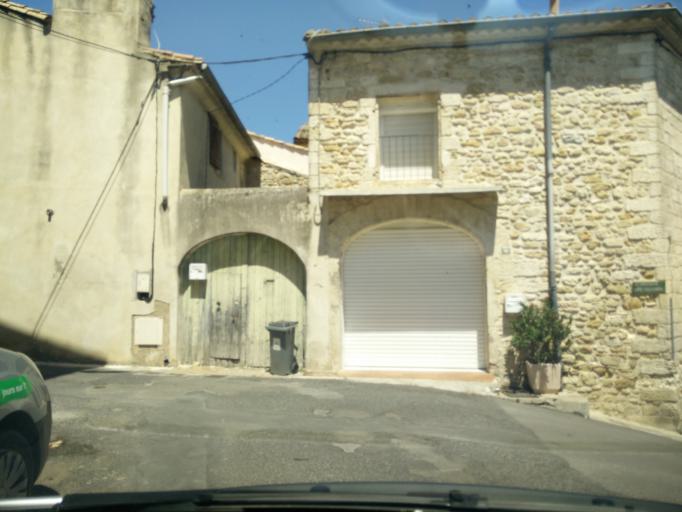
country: FR
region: Languedoc-Roussillon
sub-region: Departement de l'Herault
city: Saint-Christol
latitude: 43.7266
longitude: 4.0794
